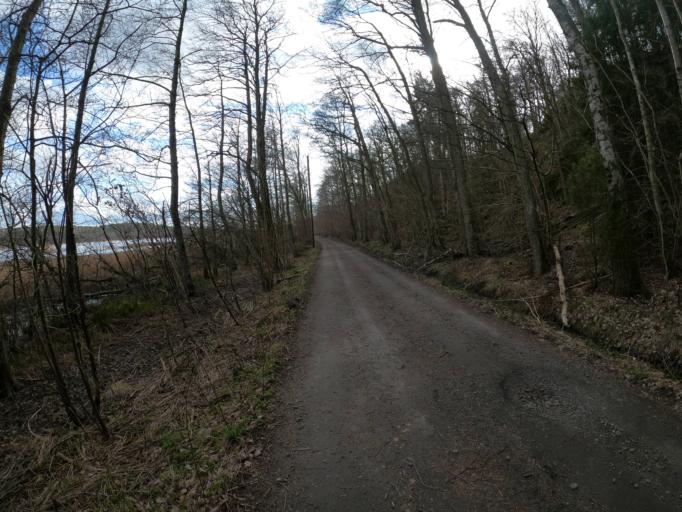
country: SE
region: Vaestra Goetaland
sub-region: Harryda Kommun
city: Molnlycke
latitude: 57.6327
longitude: 12.0976
